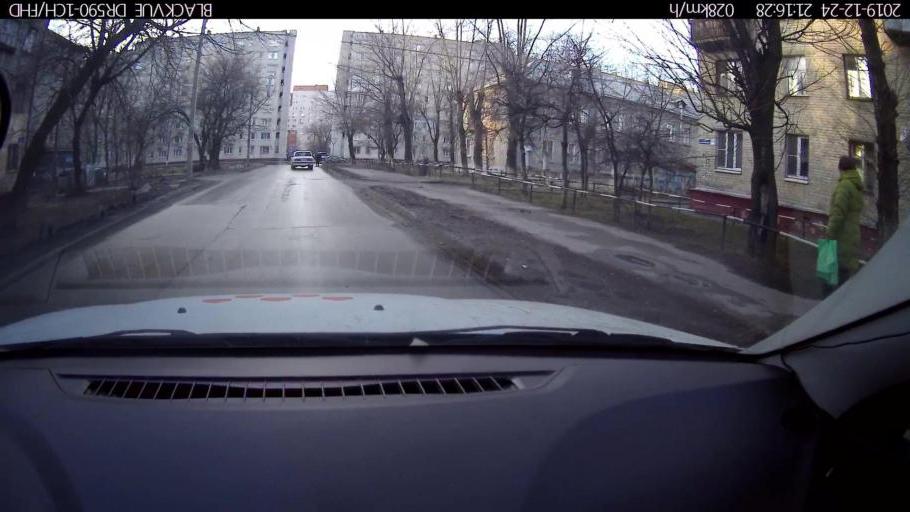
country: RU
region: Nizjnij Novgorod
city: Gorbatovka
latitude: 56.2654
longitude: 43.8779
